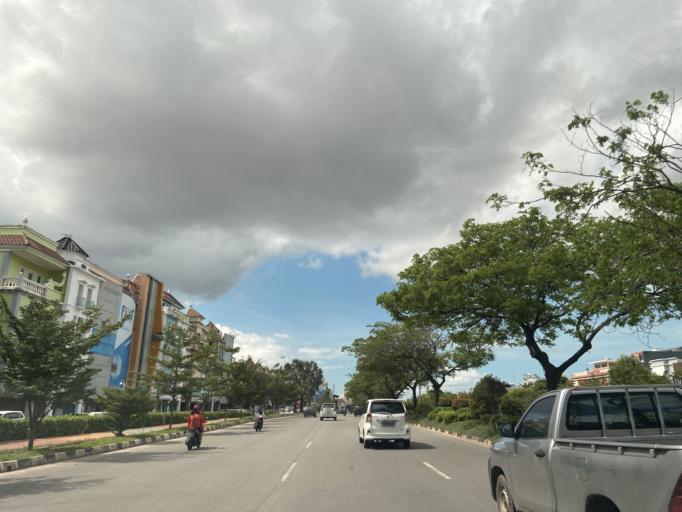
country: SG
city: Singapore
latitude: 1.1302
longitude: 104.0387
